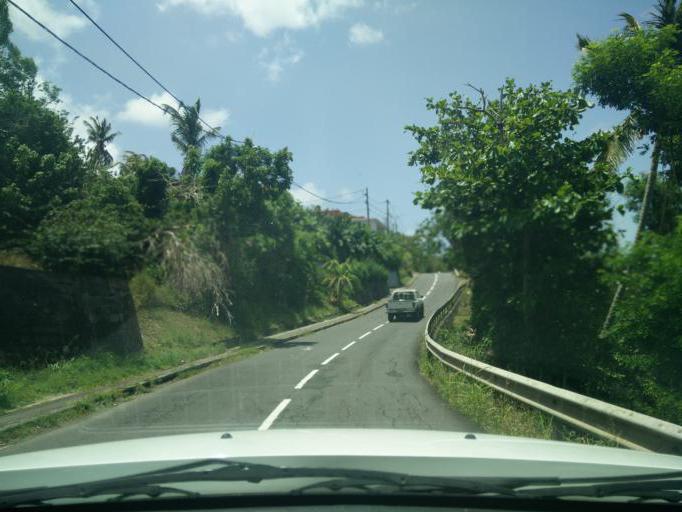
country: GP
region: Guadeloupe
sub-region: Guadeloupe
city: Gourbeyre
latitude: 15.9497
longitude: -61.7038
